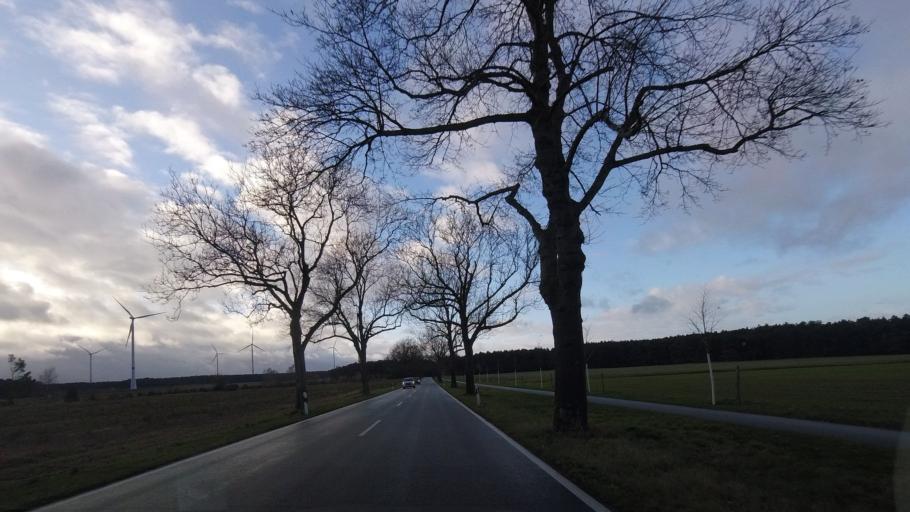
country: DE
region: Brandenburg
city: Treuenbrietzen
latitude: 52.0951
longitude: 12.8135
